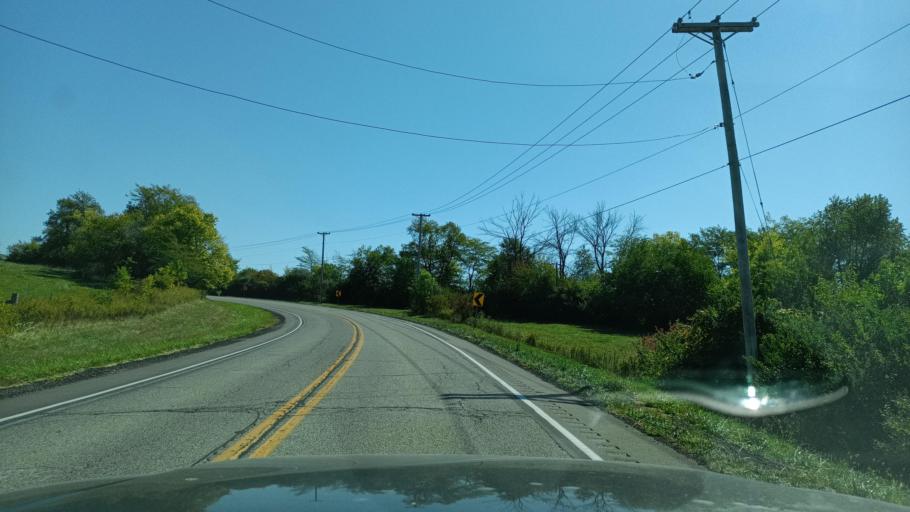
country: US
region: Illinois
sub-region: McLean County
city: Danvers
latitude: 40.6175
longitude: -89.2362
